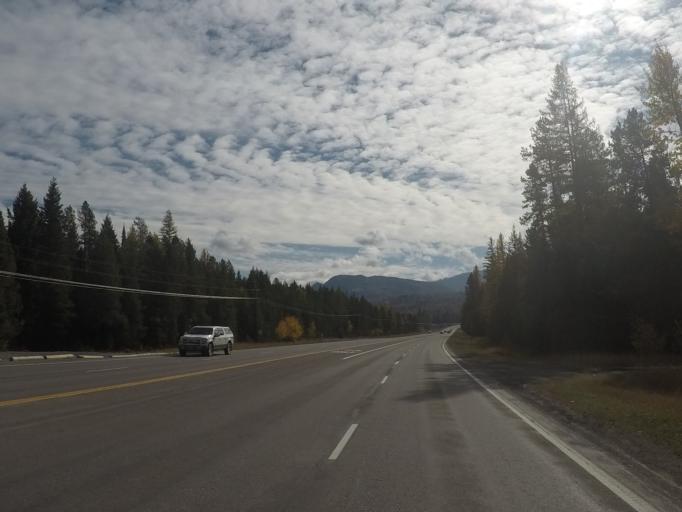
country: US
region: Montana
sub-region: Flathead County
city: Columbia Falls
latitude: 48.4064
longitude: -114.0450
